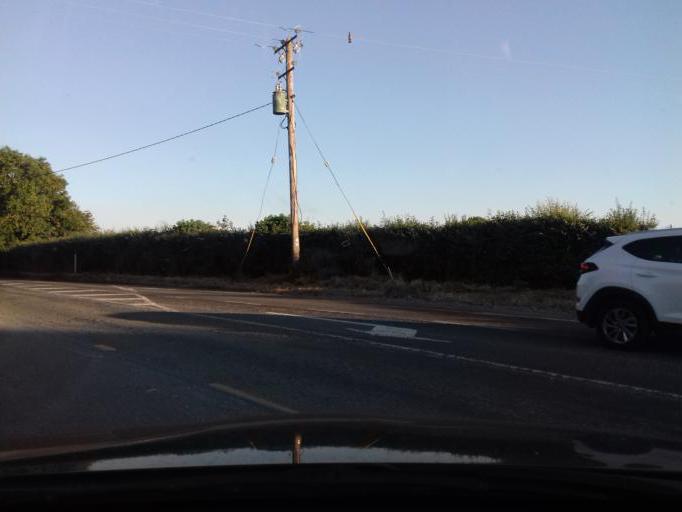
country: IE
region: Leinster
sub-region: Dublin City
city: Finglas
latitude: 53.4492
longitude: -6.3074
